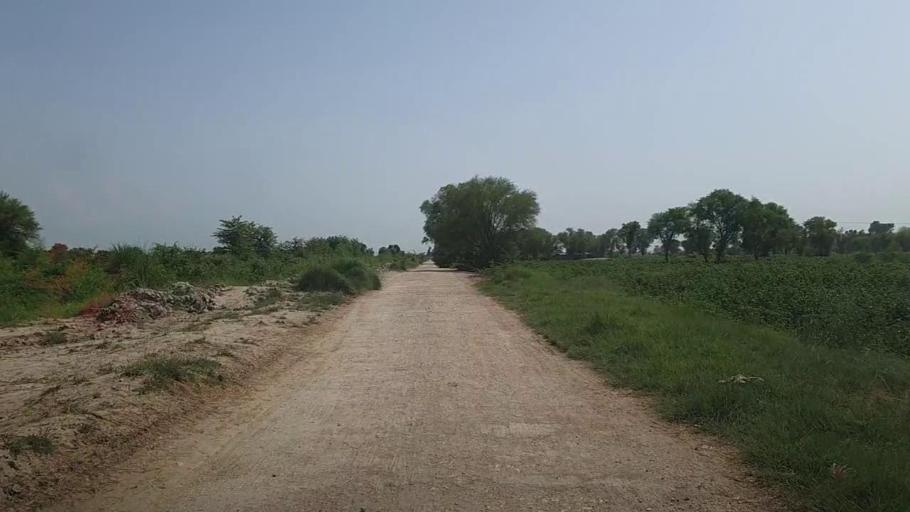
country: PK
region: Sindh
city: Pad Idan
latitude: 26.7883
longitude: 68.3263
